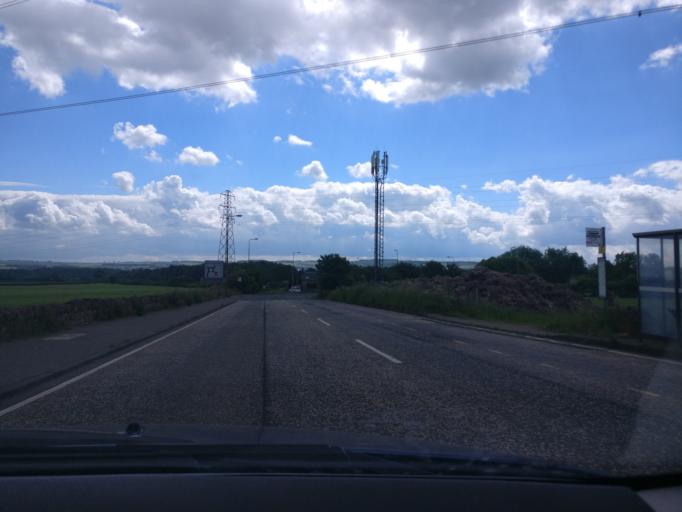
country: GB
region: Scotland
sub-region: Midlothian
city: Bonnyrigg
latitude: 55.9002
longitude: -3.1145
